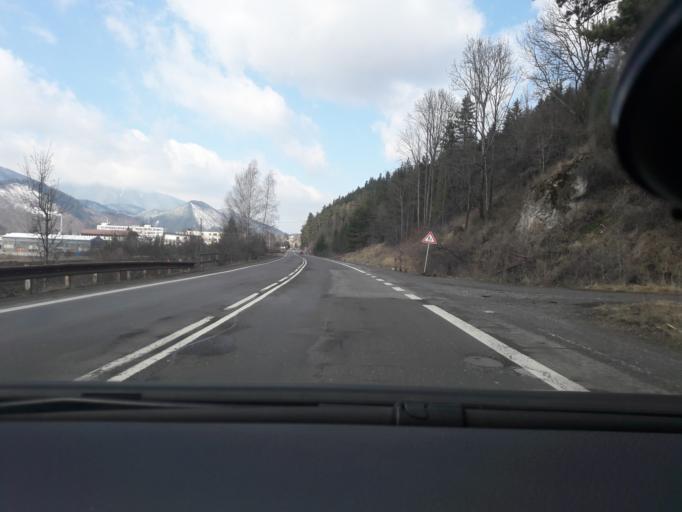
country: SK
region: Zilinsky
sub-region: Okres Zilina
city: Liptovsky Hradok
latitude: 49.0376
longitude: 19.7523
